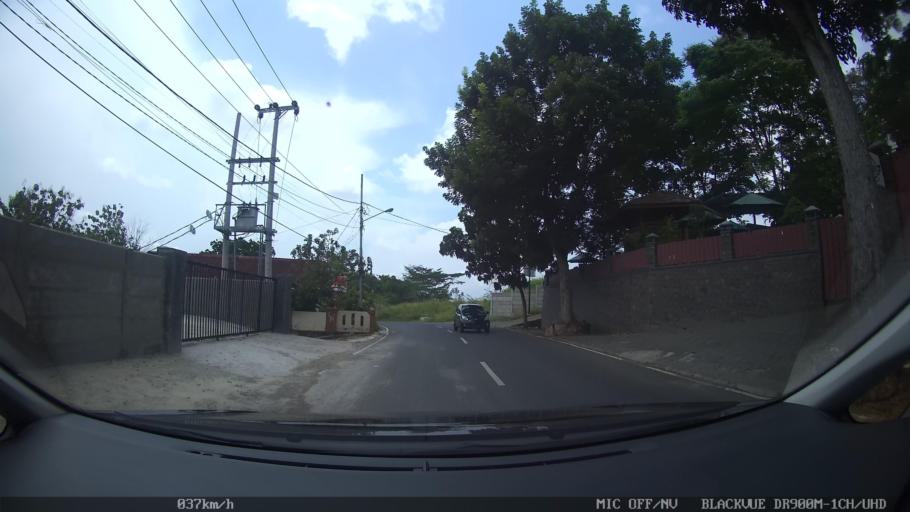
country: ID
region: Lampung
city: Bandarlampung
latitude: -5.4125
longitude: 105.2367
